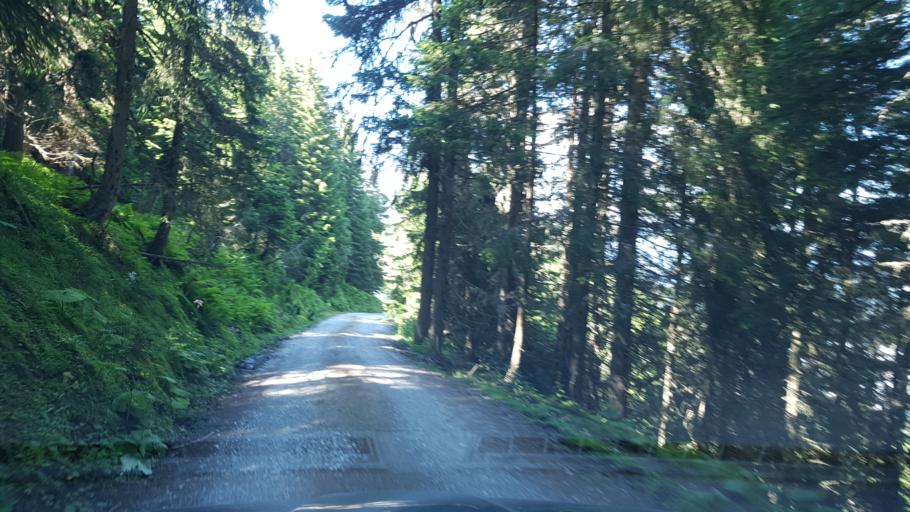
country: AT
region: Salzburg
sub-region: Politischer Bezirk Sankt Johann im Pongau
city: Dorfgastein
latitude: 47.2421
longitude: 13.0696
